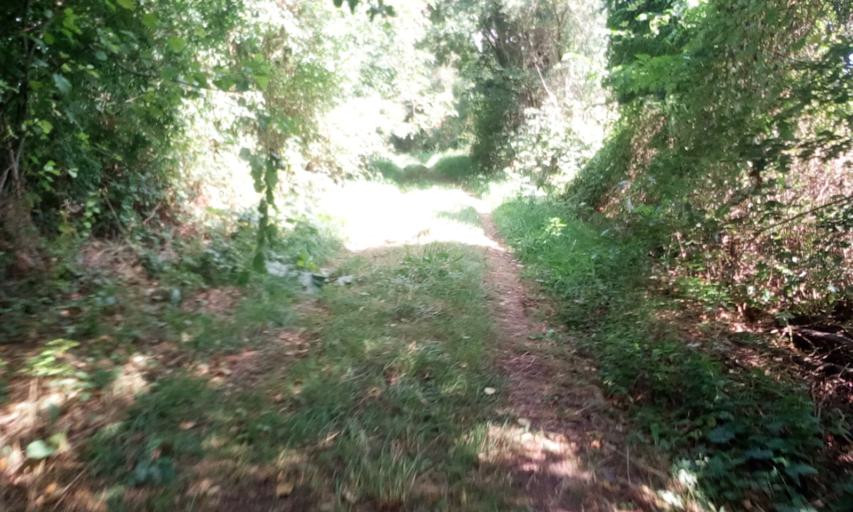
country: FR
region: Lower Normandy
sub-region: Departement du Calvados
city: Argences
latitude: 49.1271
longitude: -0.1424
